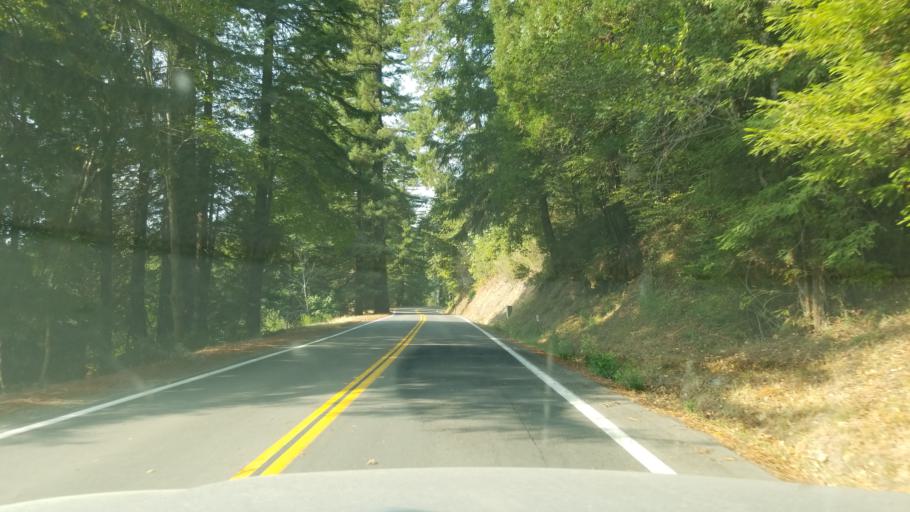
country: US
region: California
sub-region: Humboldt County
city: Redway
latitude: 40.2467
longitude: -123.8226
